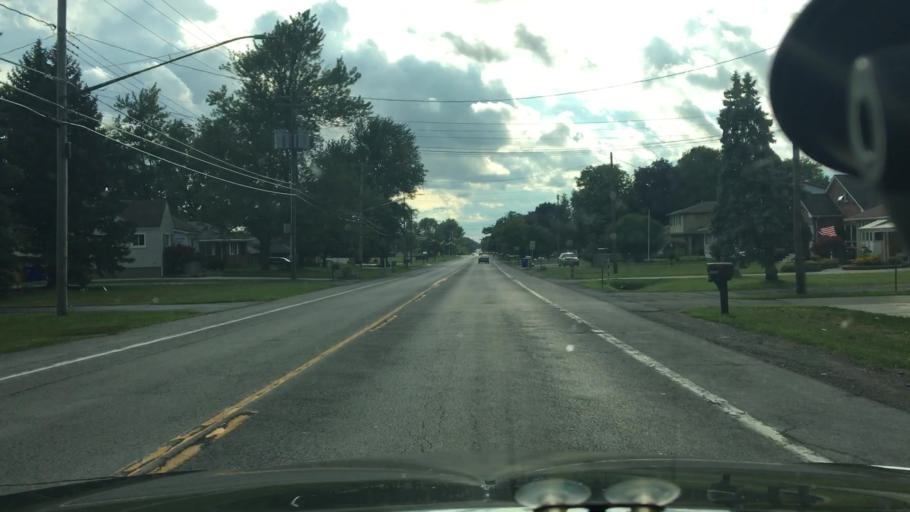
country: US
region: New York
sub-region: Erie County
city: Cheektowaga
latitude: 42.8393
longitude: -78.7256
